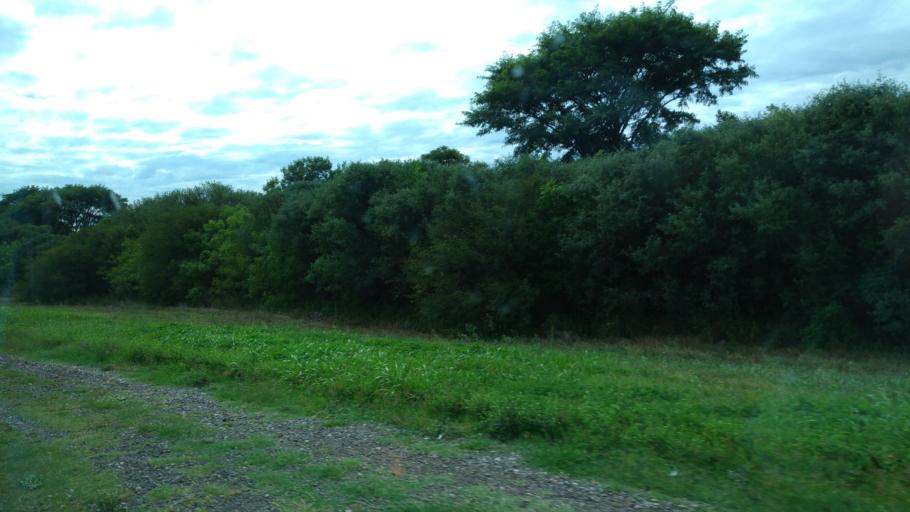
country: AR
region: Jujuy
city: La Mendieta
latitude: -24.3410
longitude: -64.9480
